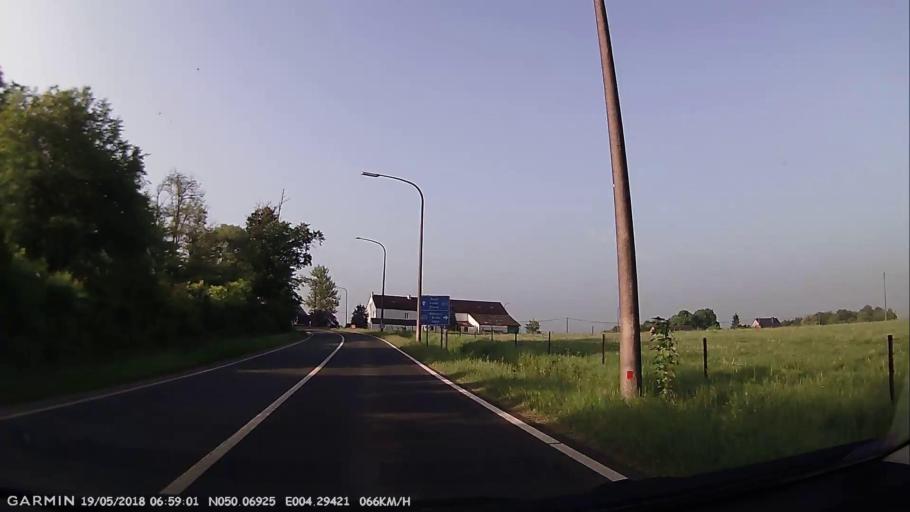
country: BE
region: Wallonia
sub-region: Province du Hainaut
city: Chimay
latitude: 50.0691
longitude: 4.2942
